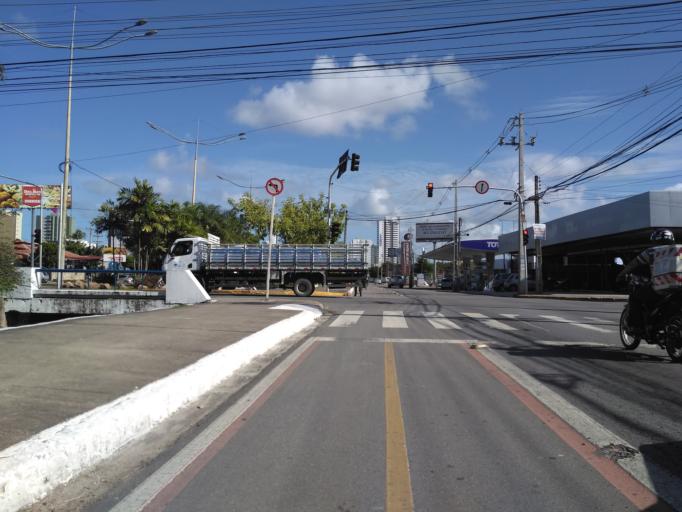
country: BR
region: Pernambuco
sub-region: Jaboatao Dos Guararapes
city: Jaboatao
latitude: -8.1656
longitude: -34.9158
